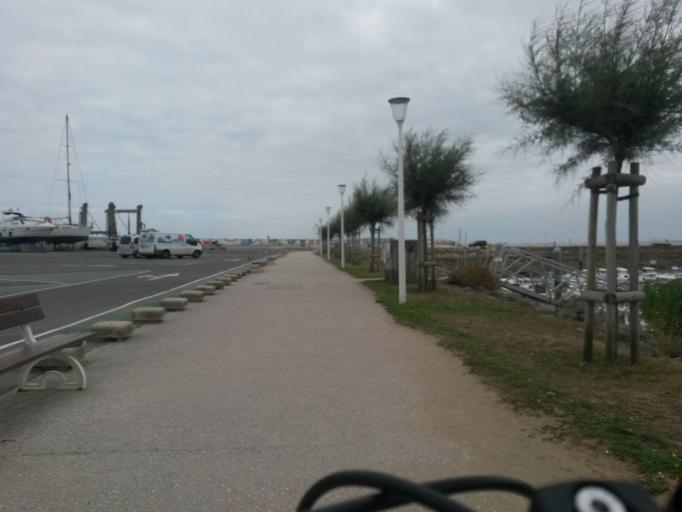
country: FR
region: Poitou-Charentes
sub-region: Departement de la Charente-Maritime
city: Saint-Denis-d'Oleron
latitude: 46.0380
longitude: -1.3708
